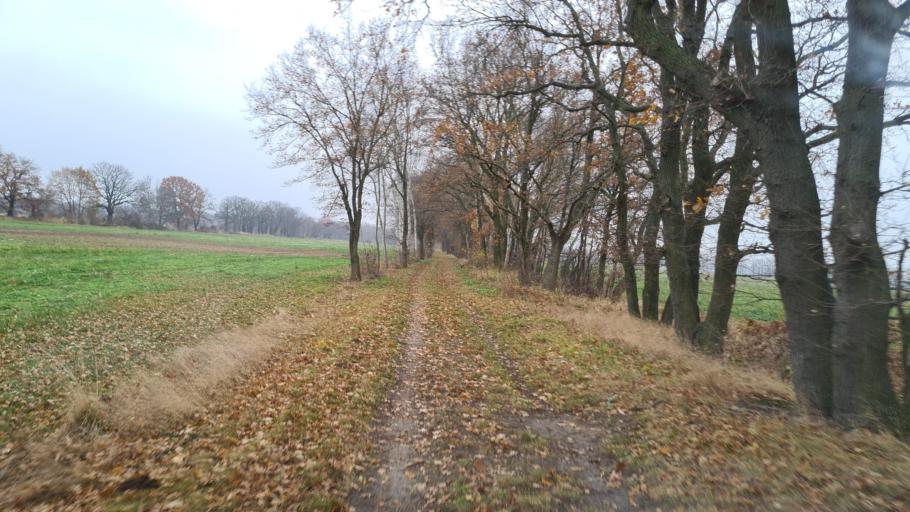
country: DE
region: Brandenburg
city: Schraden
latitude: 51.4143
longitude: 13.7117
